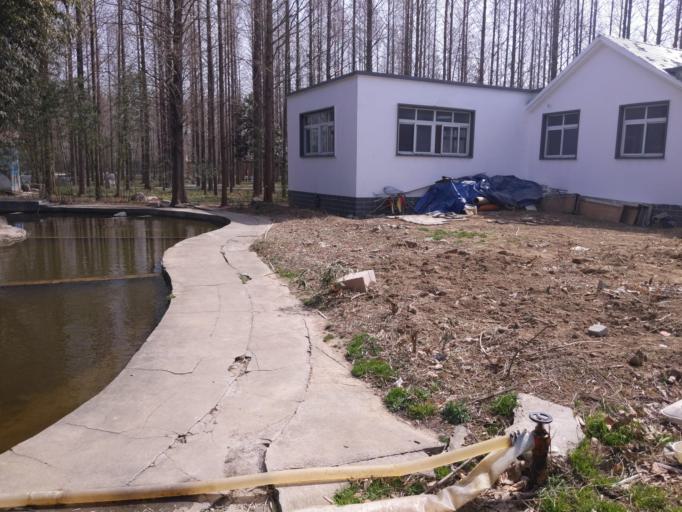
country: CN
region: Henan Sheng
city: Puyang
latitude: 35.7758
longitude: 114.9606
